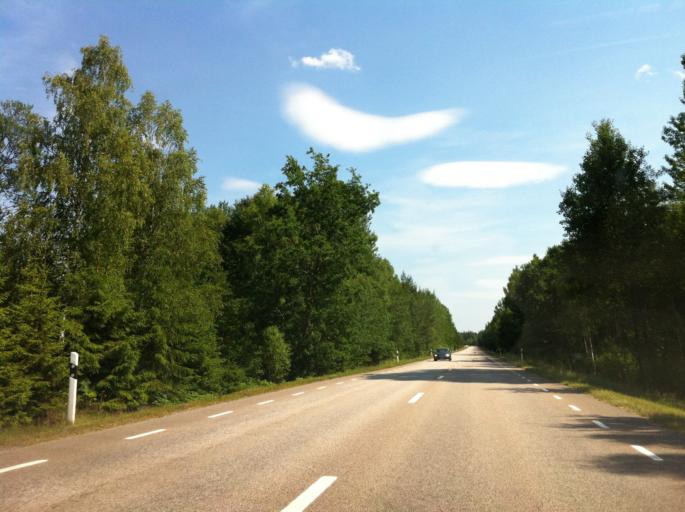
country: SE
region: Kalmar
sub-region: Nybro Kommun
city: Nybro
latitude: 56.8311
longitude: 15.7437
